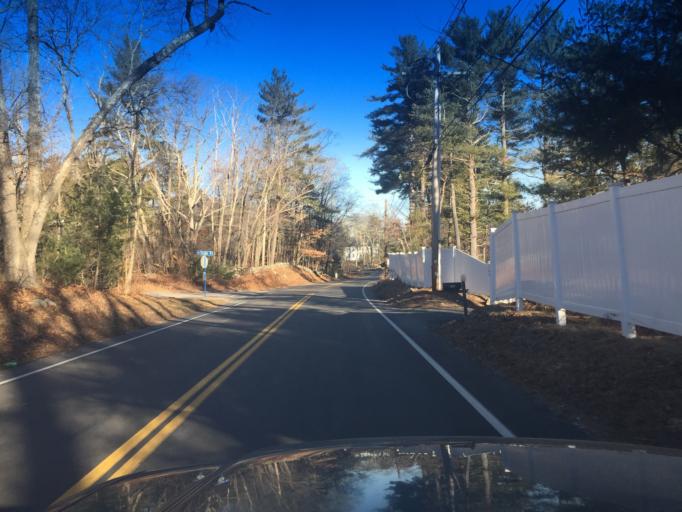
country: US
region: Massachusetts
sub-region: Middlesex County
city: Holliston
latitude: 42.1755
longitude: -71.4114
